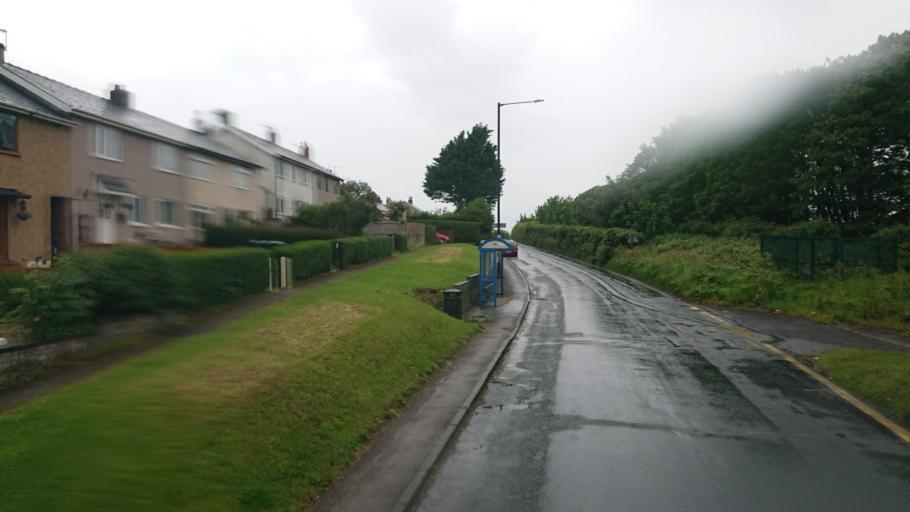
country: GB
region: England
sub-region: Lancashire
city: Morecambe
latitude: 54.0224
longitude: -2.8819
